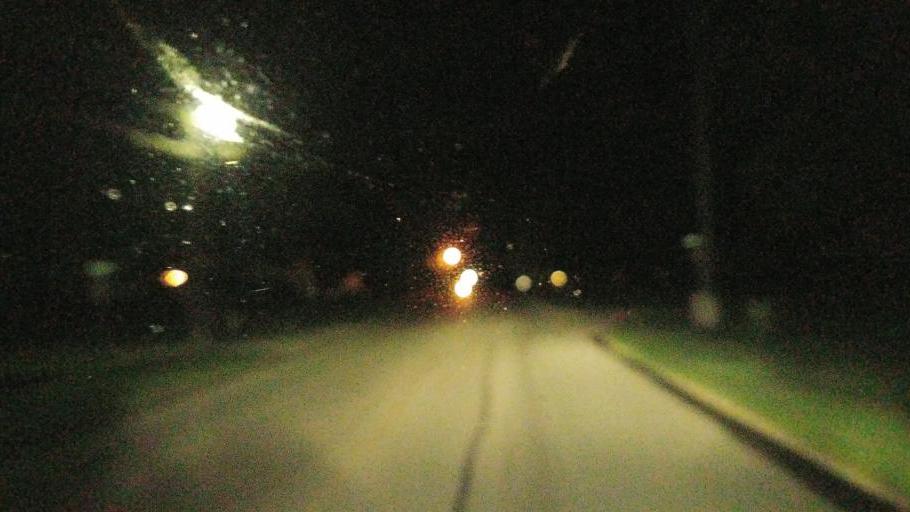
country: US
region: Iowa
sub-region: Decatur County
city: Lamoni
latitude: 40.6237
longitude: -93.9420
